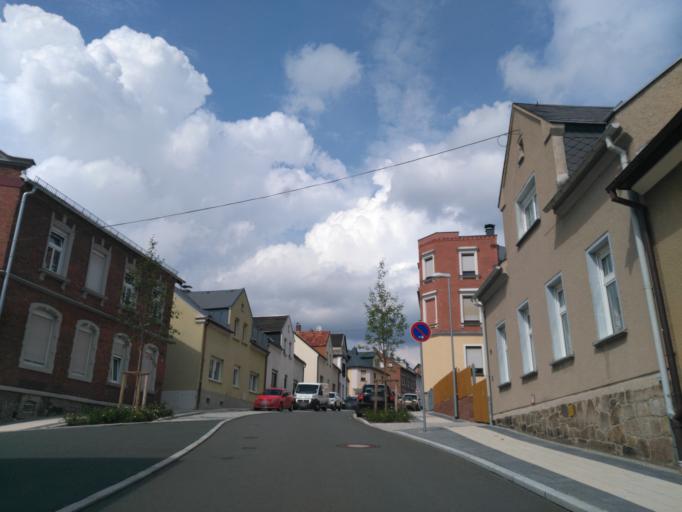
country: DE
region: Saxony
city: Rodewisch
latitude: 50.5329
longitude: 12.4120
